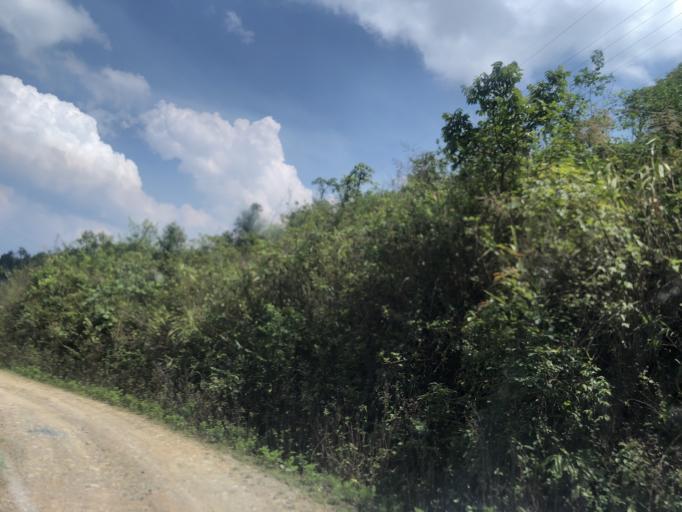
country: LA
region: Phongsali
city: Phongsali
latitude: 21.3919
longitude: 102.1916
